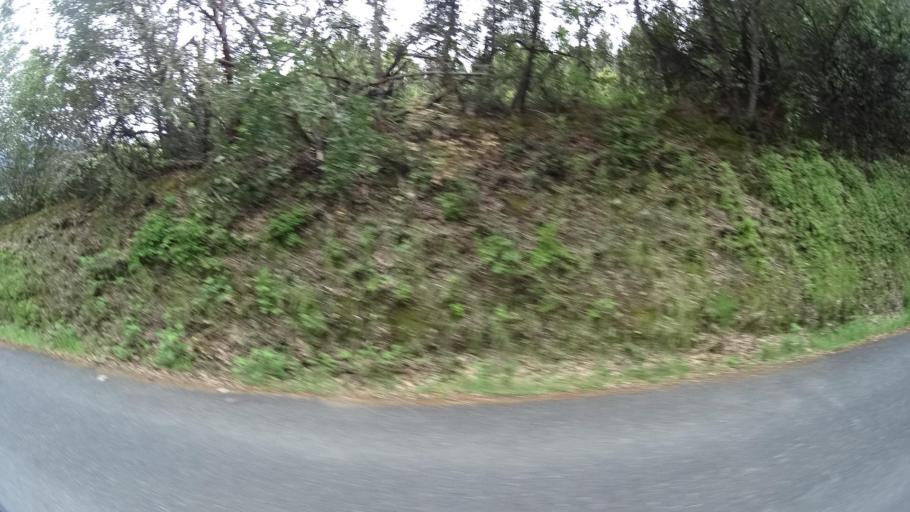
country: US
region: California
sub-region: Humboldt County
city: Willow Creek
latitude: 40.9488
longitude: -123.6217
